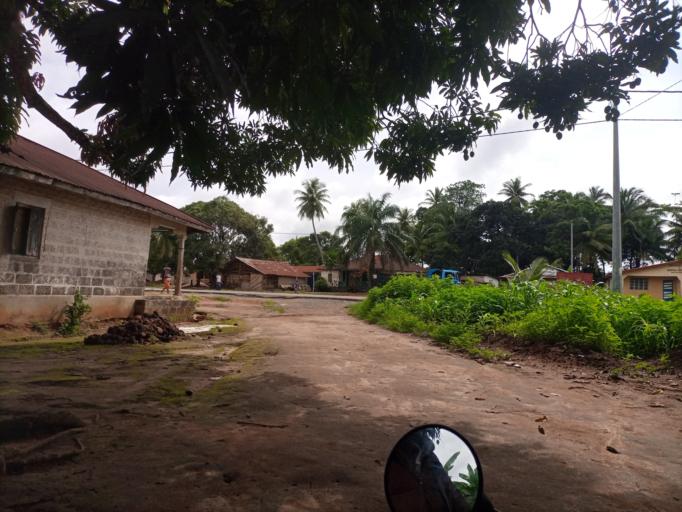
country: SL
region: Northern Province
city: Masoyila
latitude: 8.5993
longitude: -13.1745
